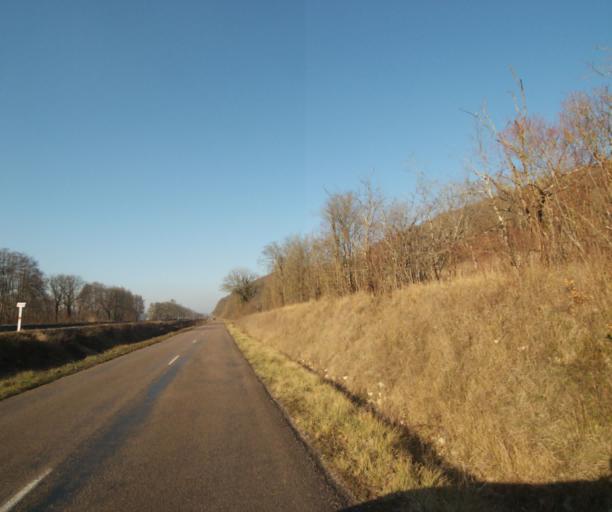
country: FR
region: Champagne-Ardenne
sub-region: Departement de la Haute-Marne
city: Chevillon
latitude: 48.5039
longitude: 5.1266
